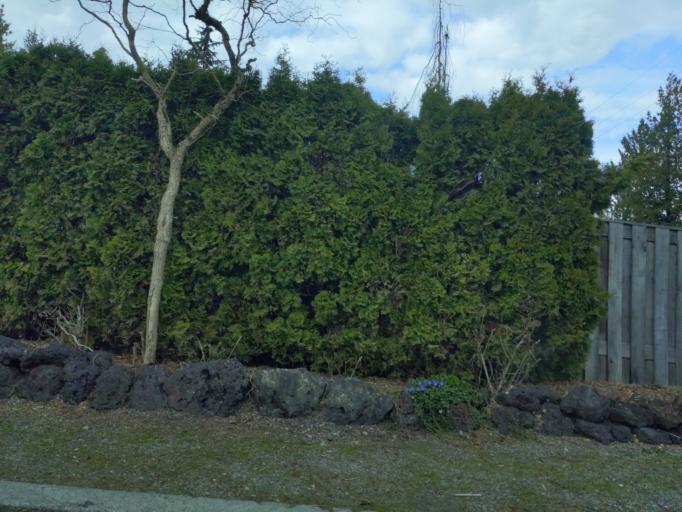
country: CA
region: British Columbia
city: Pitt Meadows
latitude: 49.2164
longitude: -122.6785
